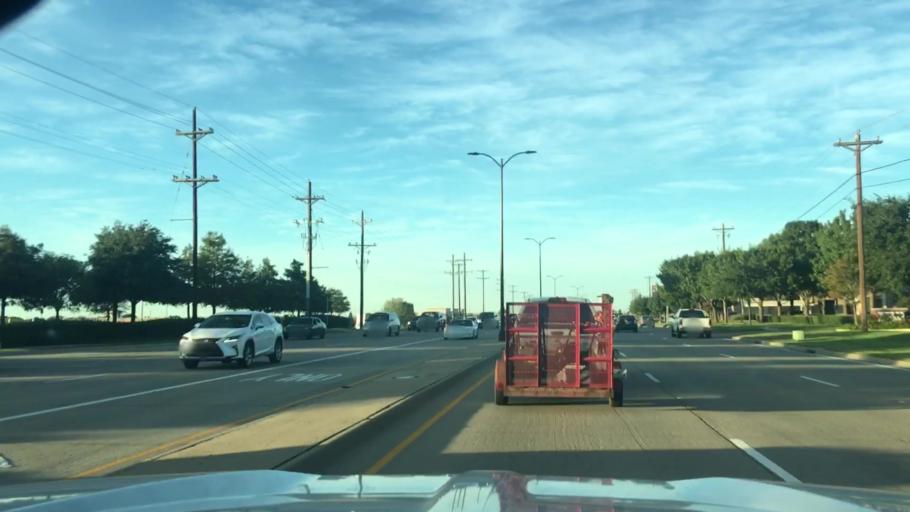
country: US
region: Texas
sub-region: Collin County
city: Frisco
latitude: 33.1413
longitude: -96.8046
